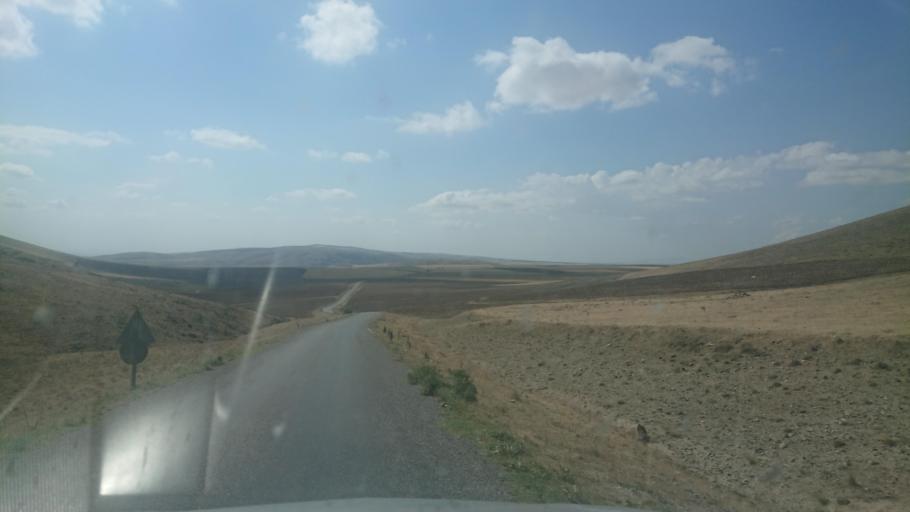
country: TR
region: Aksaray
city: Sariyahsi
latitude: 39.0007
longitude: 33.9739
